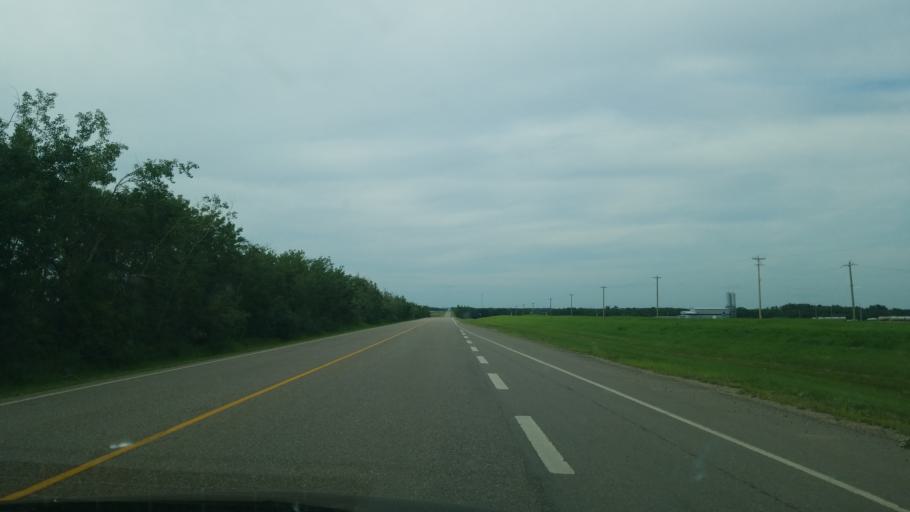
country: CA
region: Saskatchewan
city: Lloydminster
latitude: 53.3006
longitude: -110.0544
